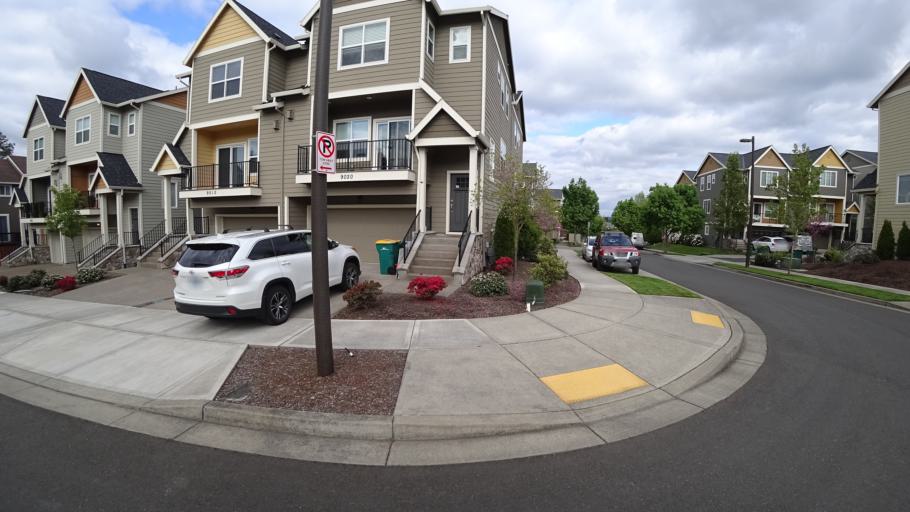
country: US
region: Oregon
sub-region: Washington County
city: Beaverton
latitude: 45.4545
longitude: -122.8376
